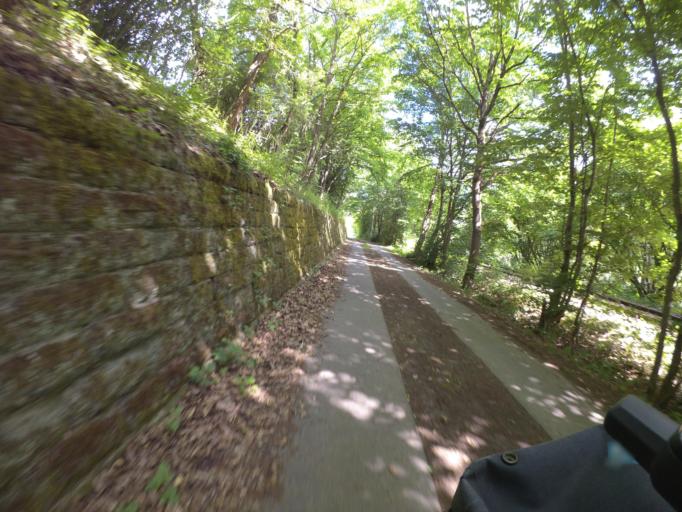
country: DE
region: Rheinland-Pfalz
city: Rehborn
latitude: 49.7411
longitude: 7.6957
